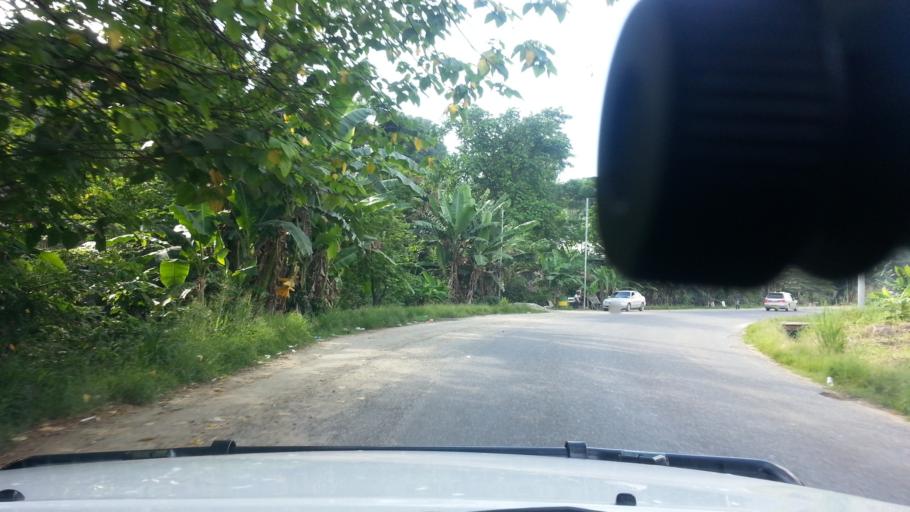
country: SB
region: Guadalcanal
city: Honiara
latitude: -9.4357
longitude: 159.9874
